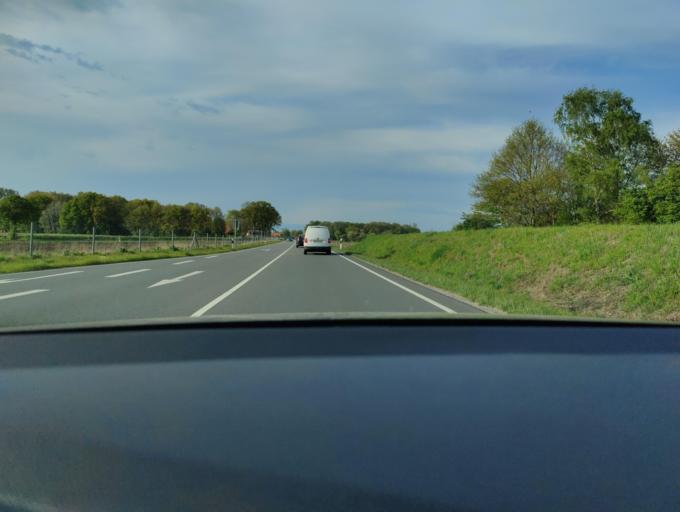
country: DE
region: Lower Saxony
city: Nordhorn
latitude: 52.4519
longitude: 7.0890
